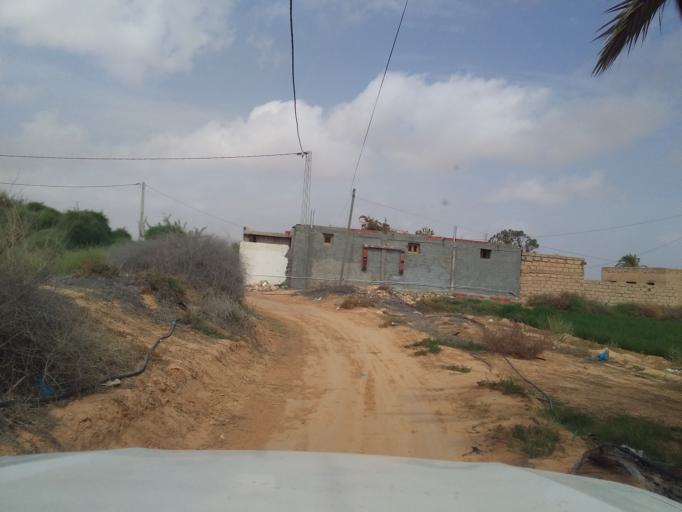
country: TN
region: Qabis
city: Gabes
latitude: 33.6261
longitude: 10.2969
